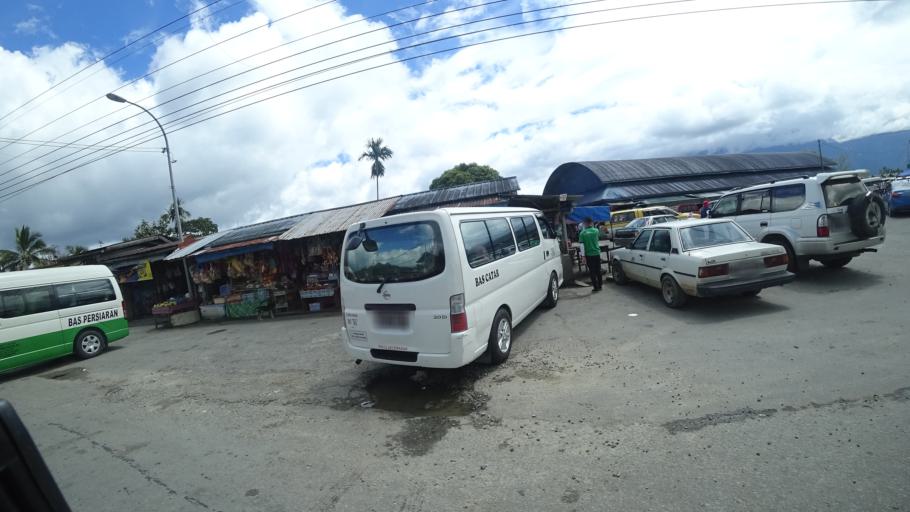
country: MY
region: Sabah
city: Ranau
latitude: 6.0280
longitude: 116.4624
